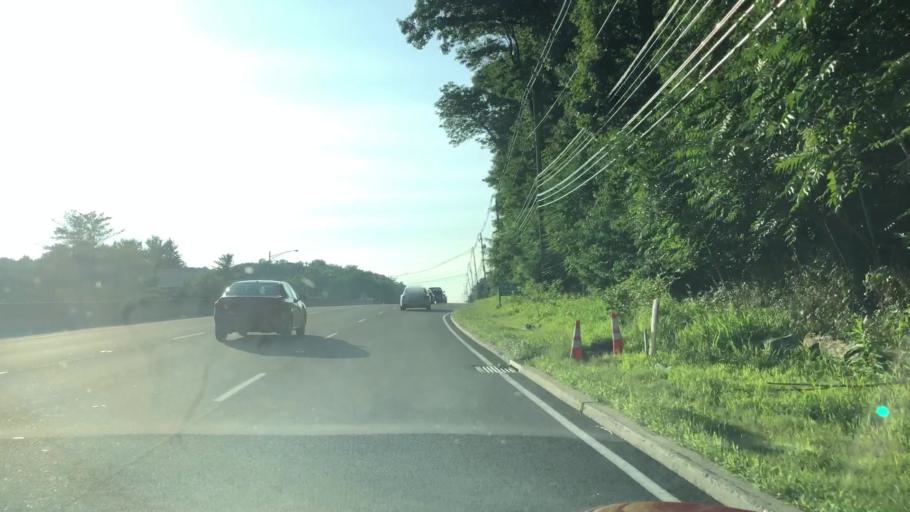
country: US
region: New Jersey
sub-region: Morris County
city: Morris Plains
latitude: 40.8566
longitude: -74.4851
